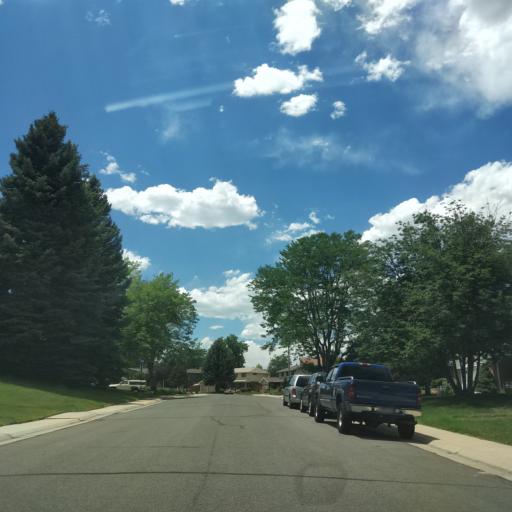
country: US
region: Colorado
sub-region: Jefferson County
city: Lakewood
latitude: 39.6889
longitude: -105.1071
